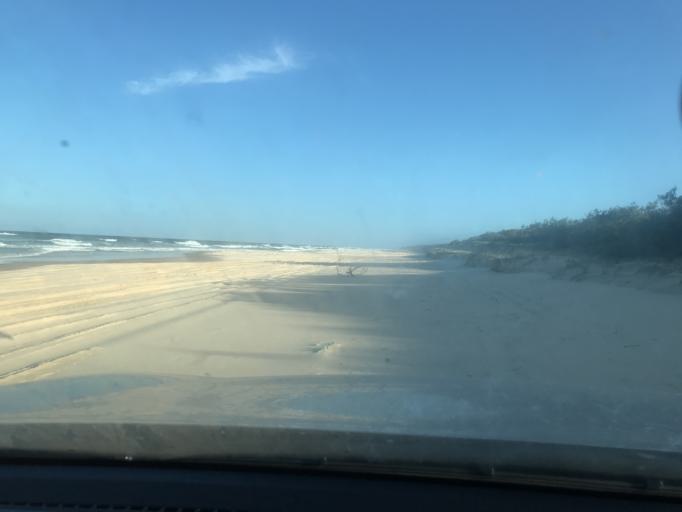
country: AU
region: Queensland
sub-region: Fraser Coast
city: Urangan
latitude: -25.3944
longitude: 153.1780
